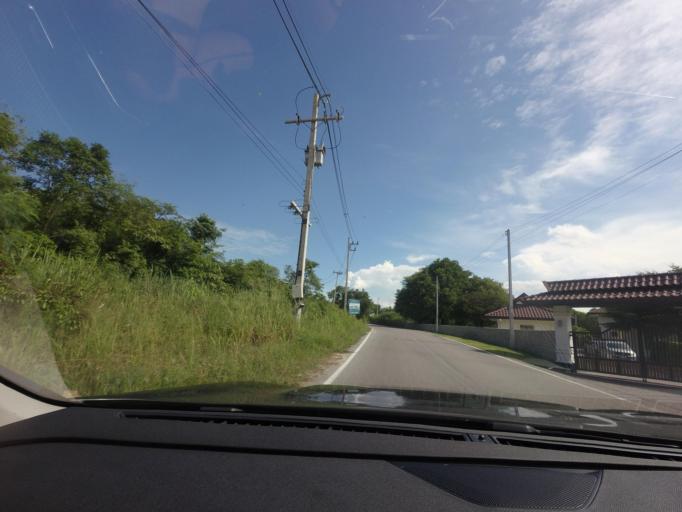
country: TH
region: Prachuap Khiri Khan
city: Hua Hin
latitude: 12.4934
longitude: 99.9415
